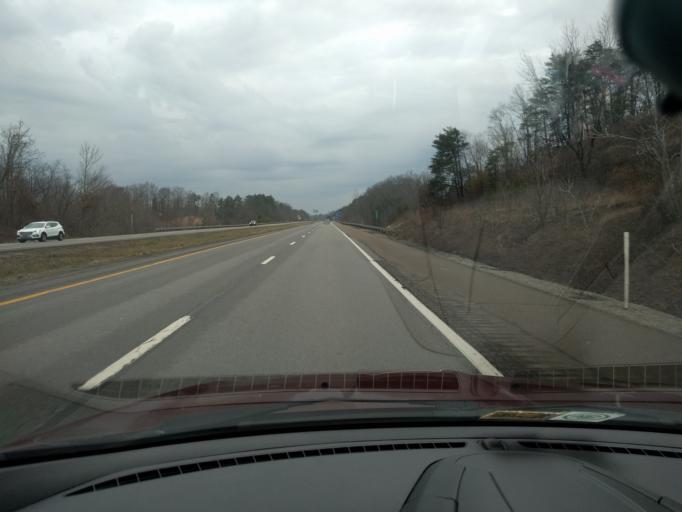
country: US
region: West Virginia
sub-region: Wood County
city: Williamstown
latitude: 39.3609
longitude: -81.4414
